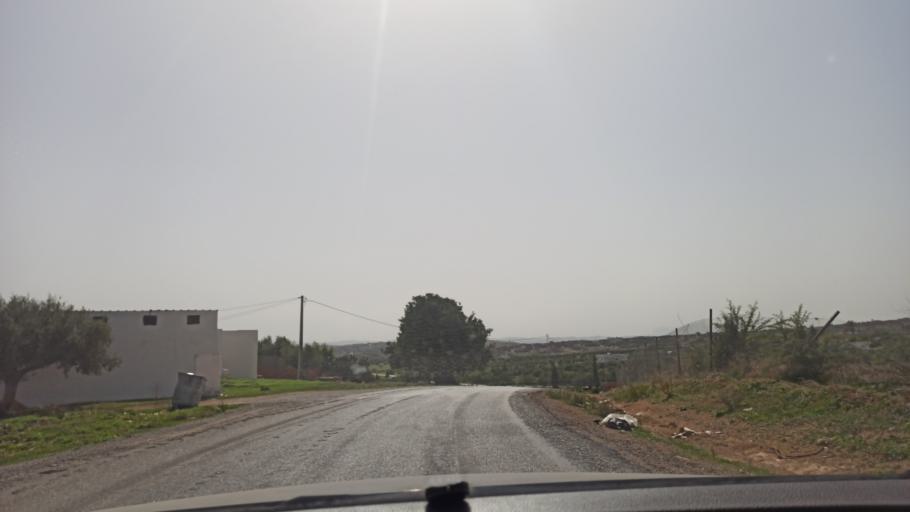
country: TN
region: Manouba
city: Manouba
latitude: 36.7336
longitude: 10.0938
